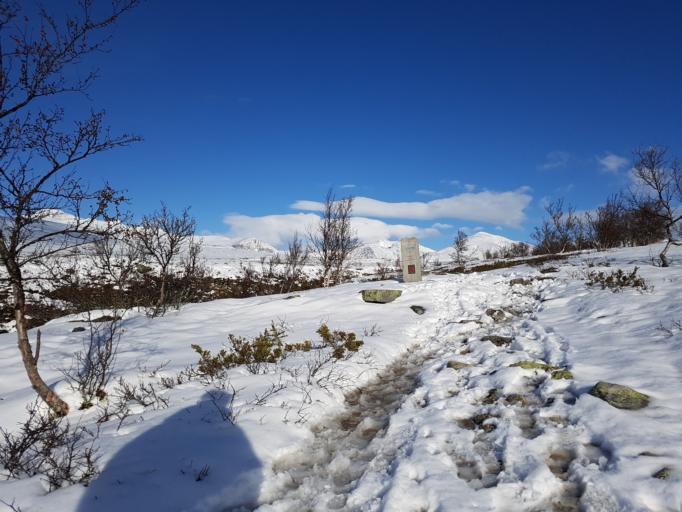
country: NO
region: Oppland
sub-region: Sel
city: Otta
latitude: 61.8299
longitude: 9.6987
